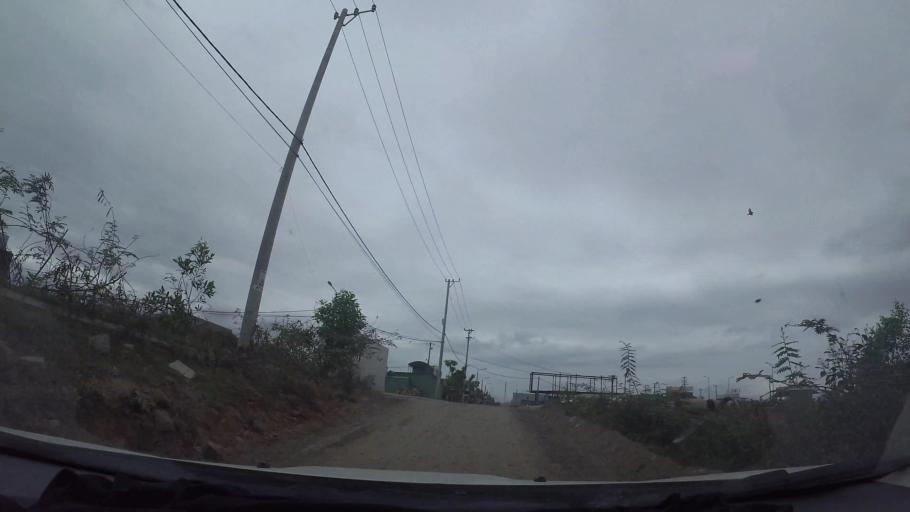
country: VN
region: Da Nang
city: Lien Chieu
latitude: 16.0907
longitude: 108.1069
